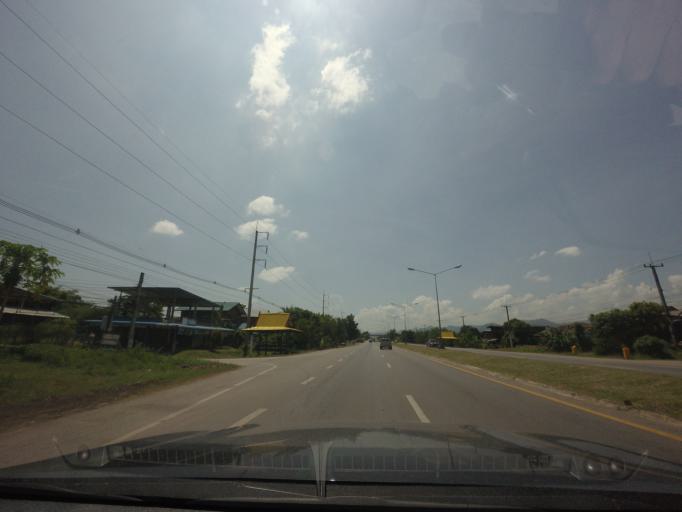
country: TH
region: Phetchabun
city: Lom Sak
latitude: 16.7042
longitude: 101.1746
